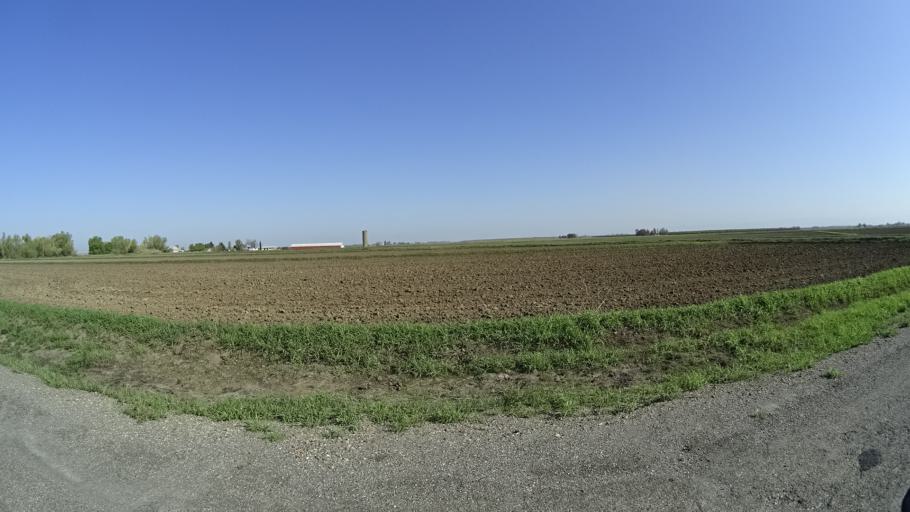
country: US
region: California
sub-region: Glenn County
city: Hamilton City
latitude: 39.6015
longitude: -122.0527
